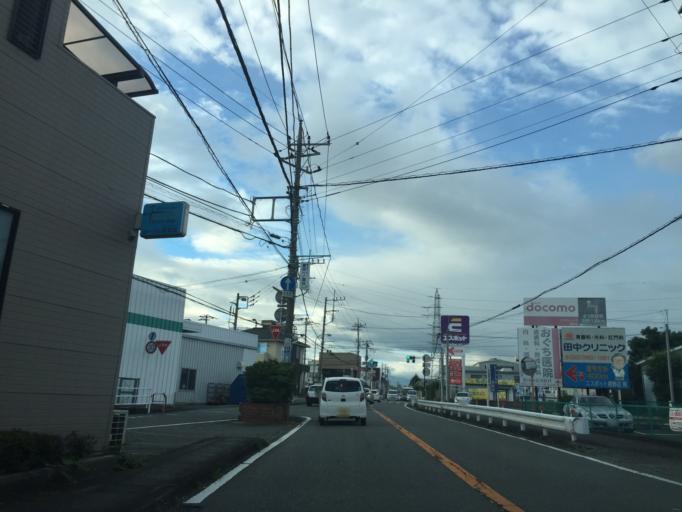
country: JP
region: Shizuoka
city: Mishima
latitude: 35.1570
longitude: 138.9077
